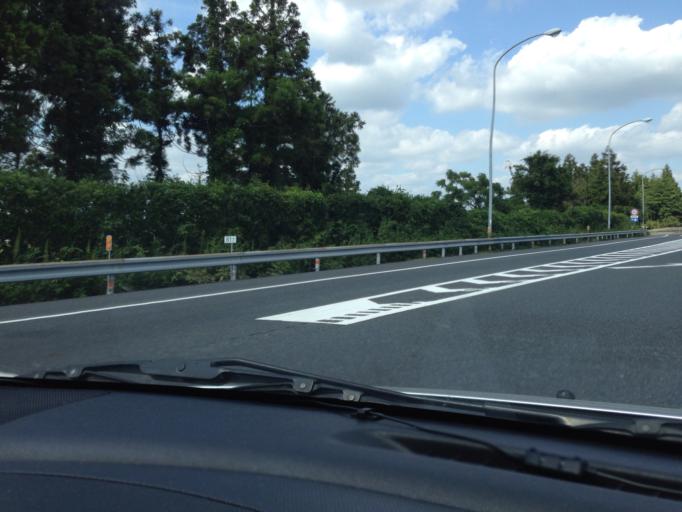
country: JP
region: Ibaraki
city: Mito-shi
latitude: 36.3800
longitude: 140.3859
